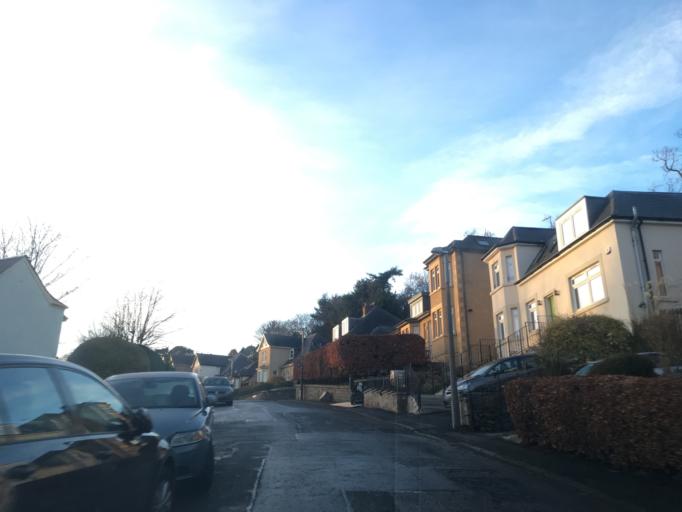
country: GB
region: Scotland
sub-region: Edinburgh
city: Colinton
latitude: 55.9458
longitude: -3.2534
